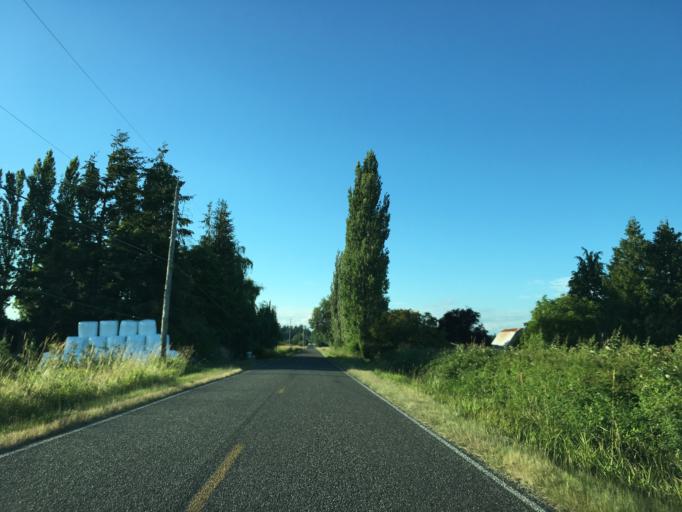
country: US
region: Washington
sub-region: Whatcom County
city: Lynden
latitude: 48.9680
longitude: -122.5301
